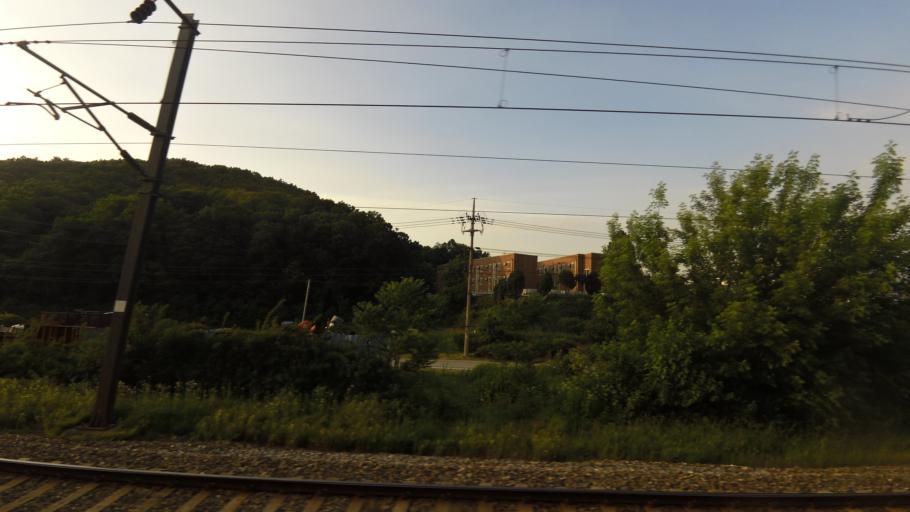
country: KR
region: Chungcheongnam-do
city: Cheonan
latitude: 36.6650
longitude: 127.2524
